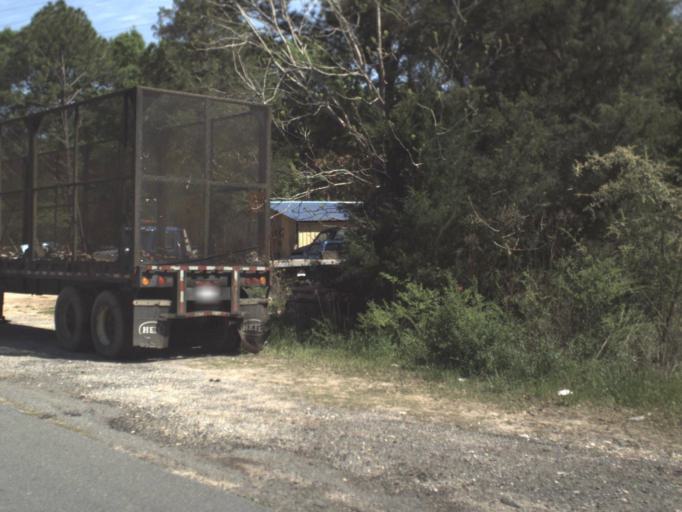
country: US
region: Florida
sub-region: Okaloosa County
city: Crestview
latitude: 30.7241
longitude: -86.7089
